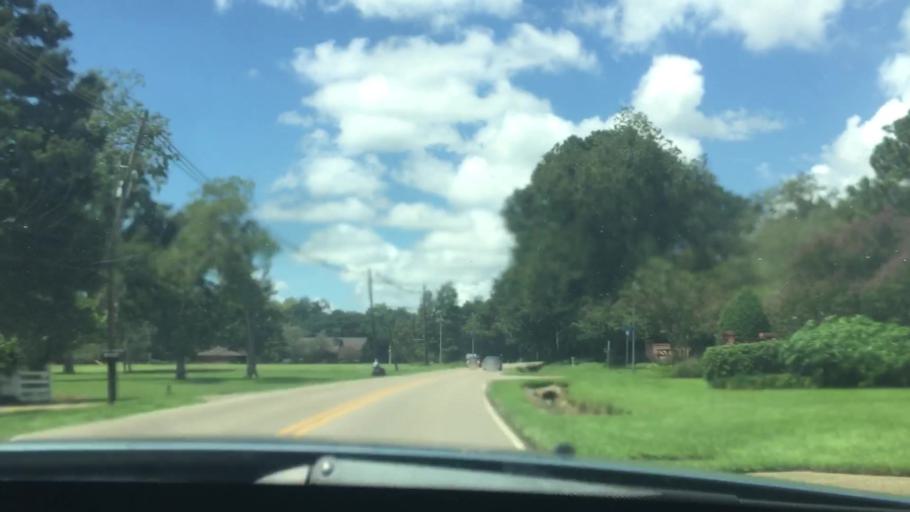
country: US
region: Louisiana
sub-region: East Baton Rouge Parish
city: Oak Hills Place
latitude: 30.3614
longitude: -91.1095
